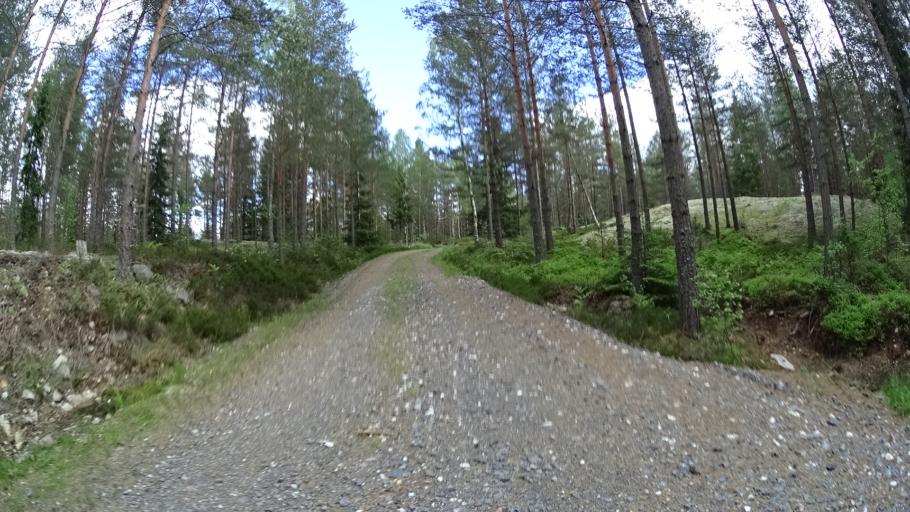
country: FI
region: Varsinais-Suomi
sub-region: Salo
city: Kisko
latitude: 60.1839
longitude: 23.5524
